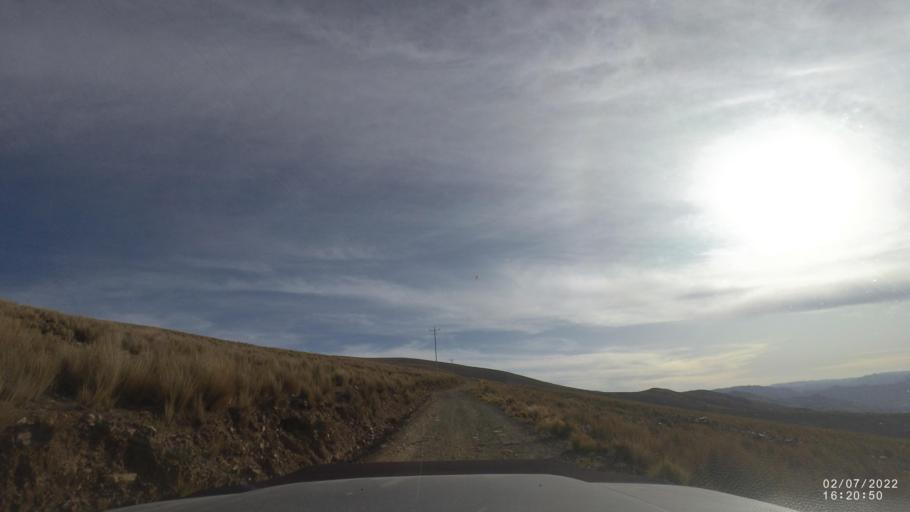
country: BO
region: Cochabamba
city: Irpa Irpa
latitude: -17.9307
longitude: -66.4494
